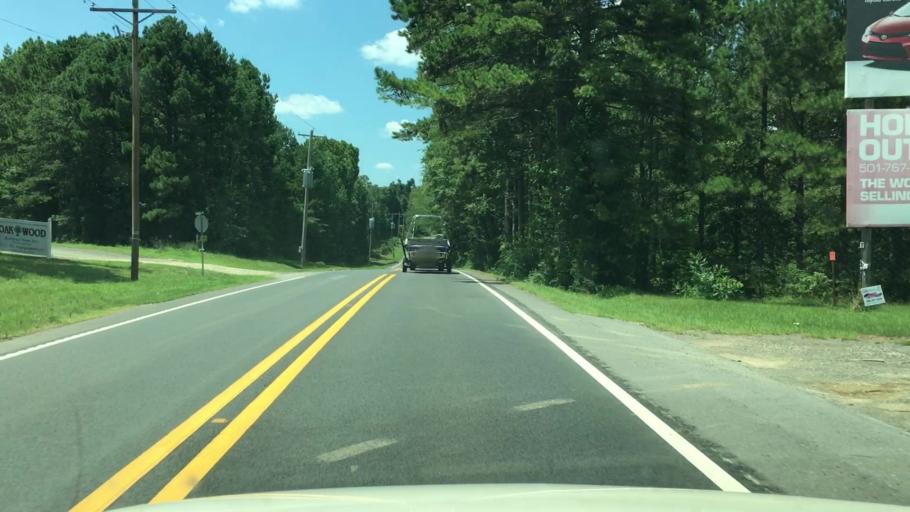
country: US
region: Arkansas
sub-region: Garland County
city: Lake Hamilton
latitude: 34.2704
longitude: -93.1460
